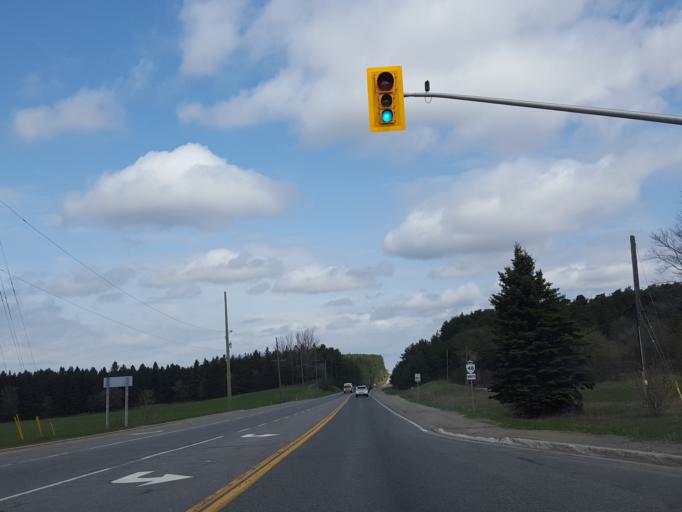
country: CA
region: Ontario
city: Newmarket
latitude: 44.0751
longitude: -79.3060
